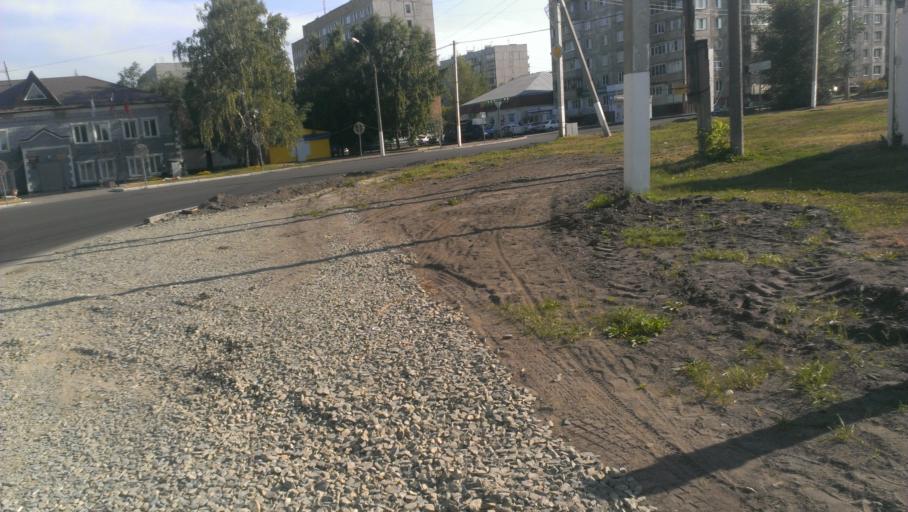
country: RU
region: Altai Krai
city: Novosilikatnyy
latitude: 53.3087
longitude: 83.6227
